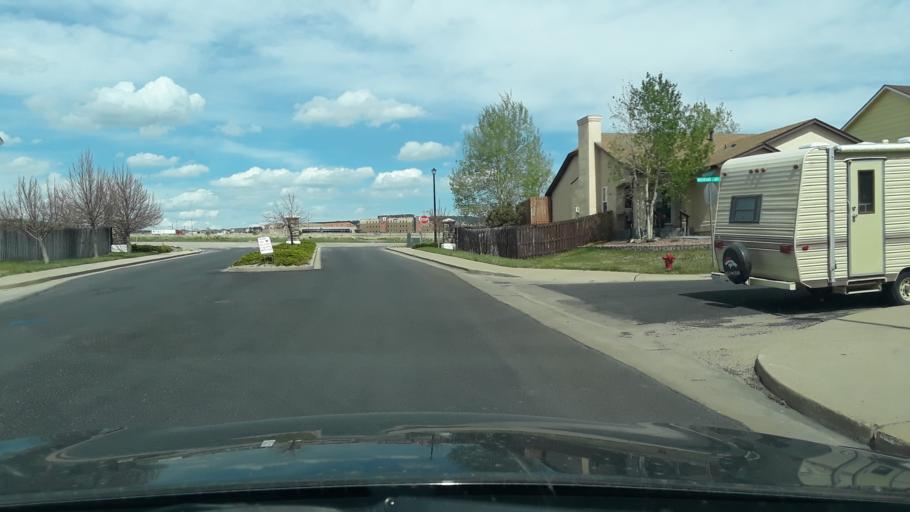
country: US
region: Colorado
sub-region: El Paso County
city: Monument
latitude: 39.0805
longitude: -104.8662
